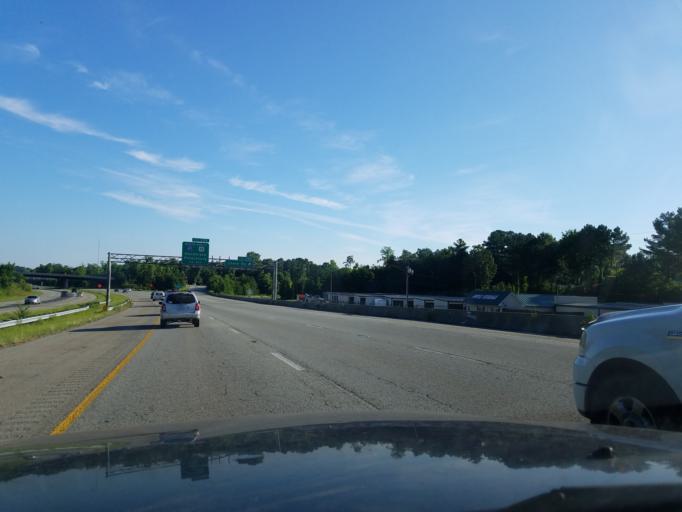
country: US
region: North Carolina
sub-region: Durham County
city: Durham
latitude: 36.0018
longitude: -78.8632
